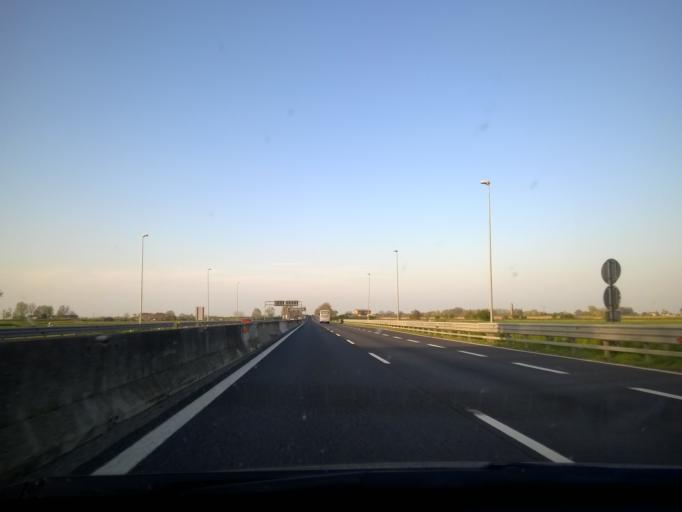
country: IT
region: Emilia-Romagna
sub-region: Provincia di Bologna
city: Altedo
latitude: 44.6900
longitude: 11.4816
